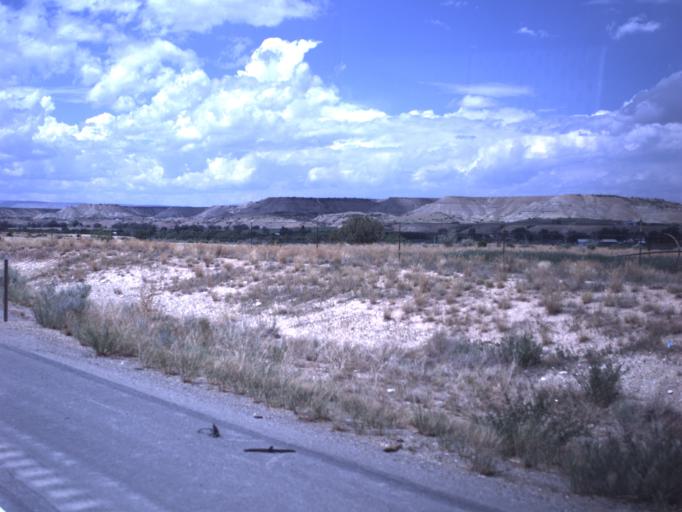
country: US
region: Utah
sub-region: Duchesne County
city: Duchesne
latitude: 40.1699
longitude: -110.3214
